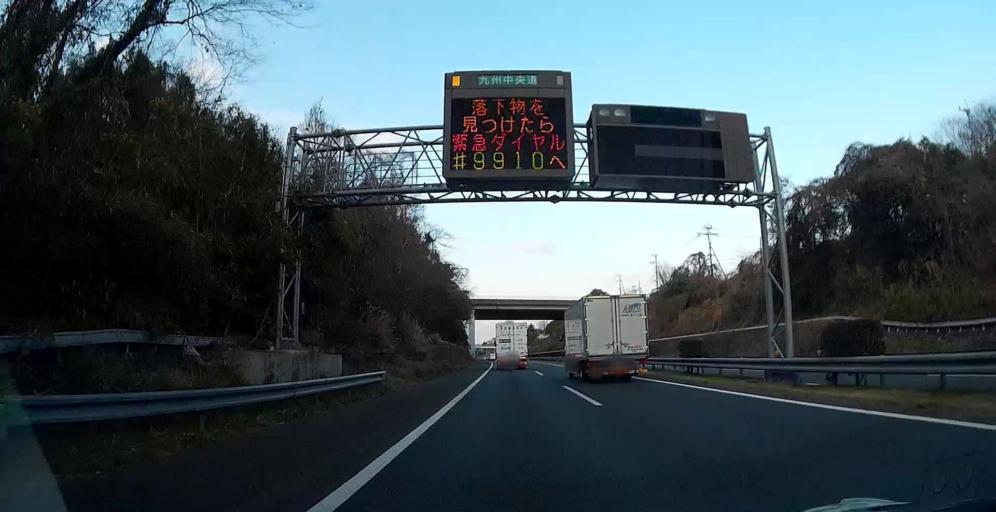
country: JP
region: Kumamoto
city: Kumamoto
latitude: 32.7472
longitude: 130.7870
